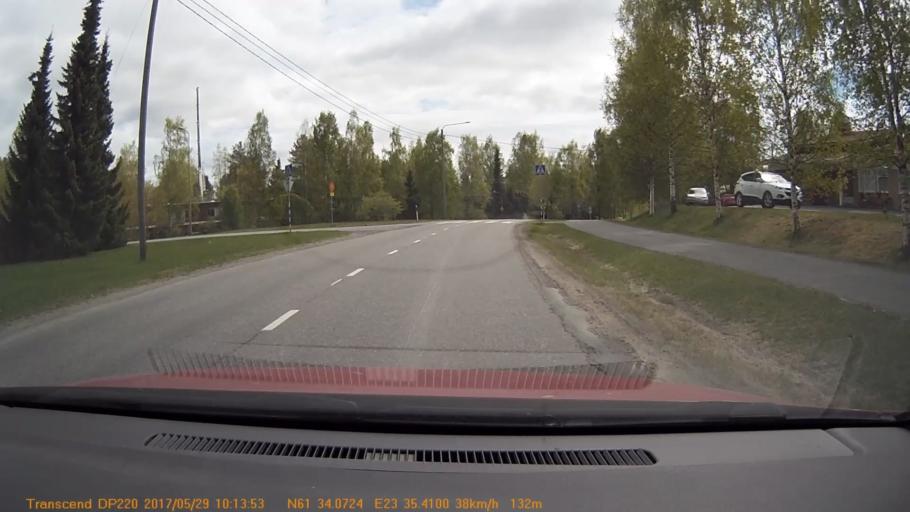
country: FI
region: Pirkanmaa
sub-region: Tampere
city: Yloejaervi
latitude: 61.5680
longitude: 23.5900
